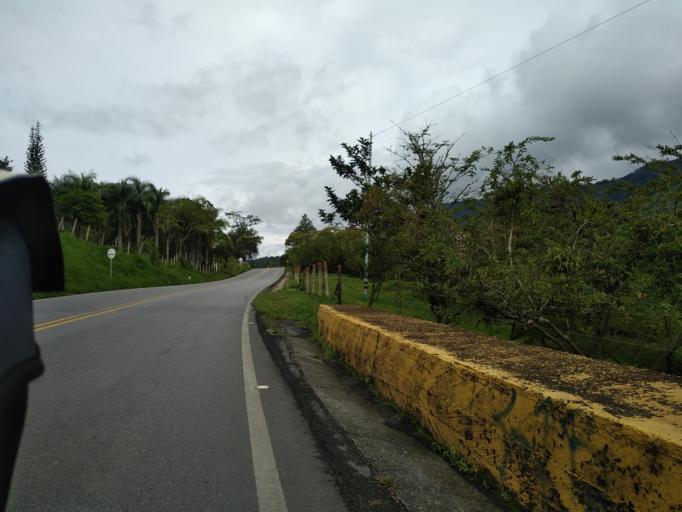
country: CO
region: Santander
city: Suaita
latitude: 6.0976
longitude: -73.3797
